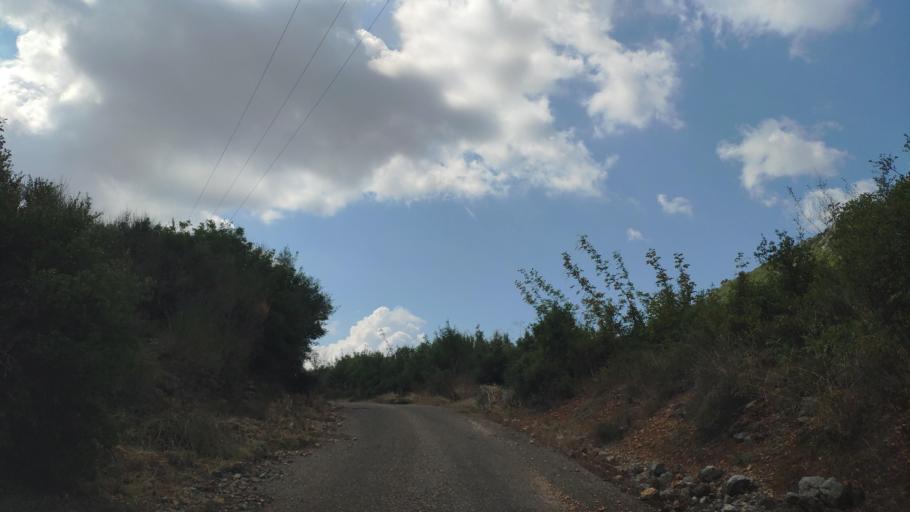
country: GR
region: West Greece
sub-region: Nomos Aitolias kai Akarnanias
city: Fitiai
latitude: 38.6686
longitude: 21.1435
